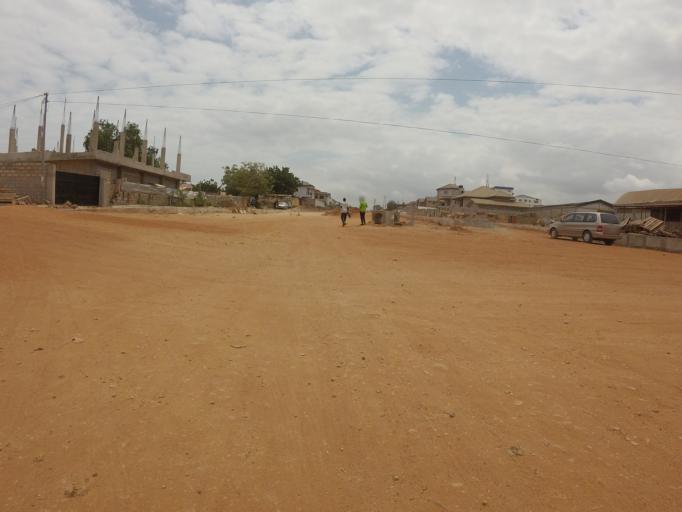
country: GH
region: Greater Accra
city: Medina Estates
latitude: 5.6301
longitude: -0.1403
